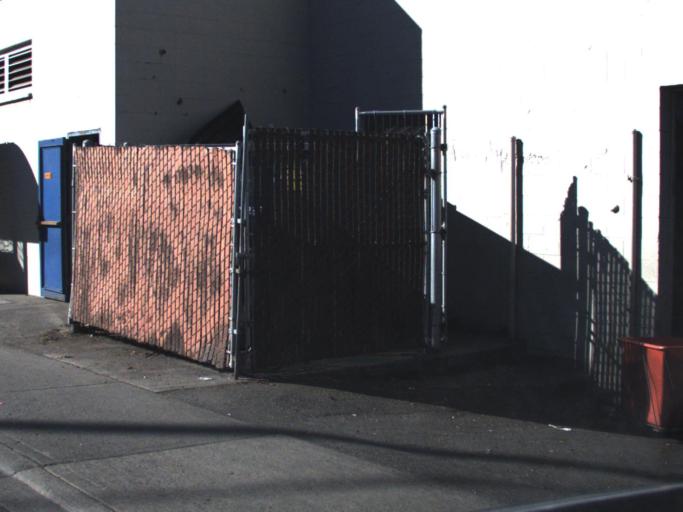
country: US
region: Washington
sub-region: King County
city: Renton
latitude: 47.4780
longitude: -122.2042
